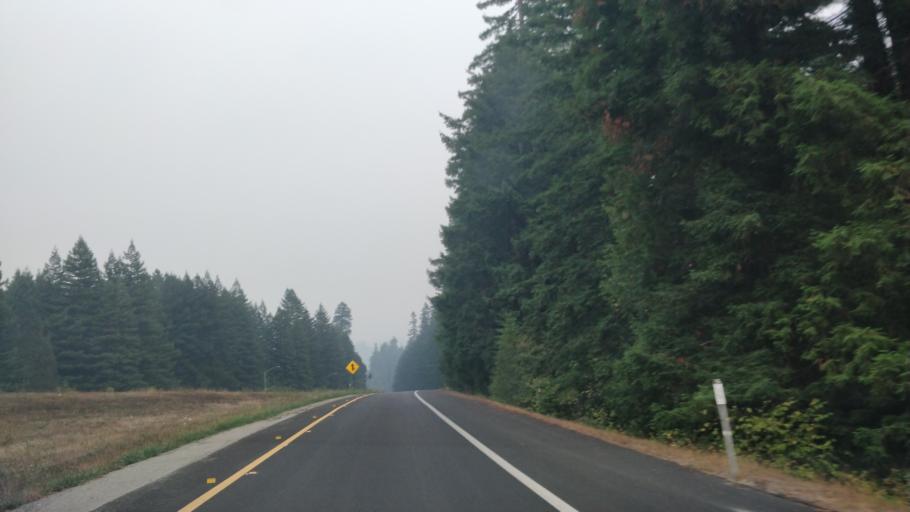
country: US
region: California
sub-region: Humboldt County
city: Rio Dell
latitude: 40.3970
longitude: -123.9478
